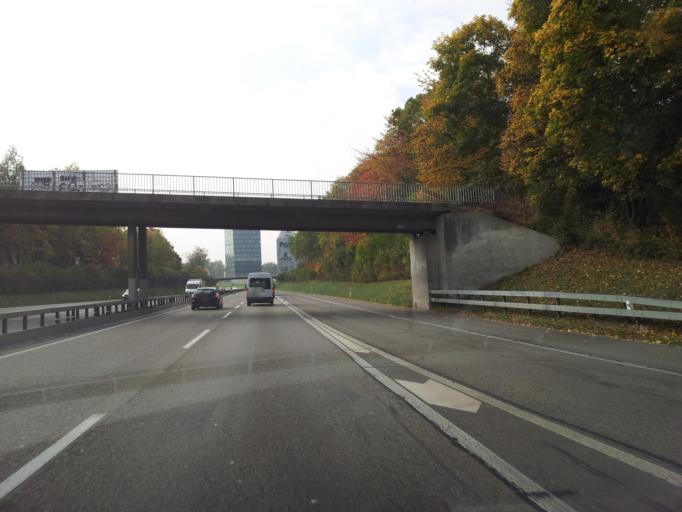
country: CH
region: Bern
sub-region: Bern-Mittelland District
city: Bern
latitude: 46.9601
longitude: 7.4730
